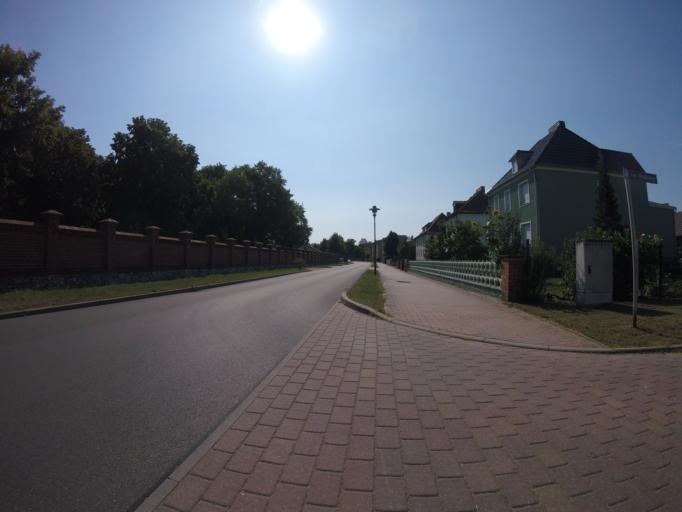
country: DE
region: Brandenburg
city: Mullrose
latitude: 52.2440
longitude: 14.4101
